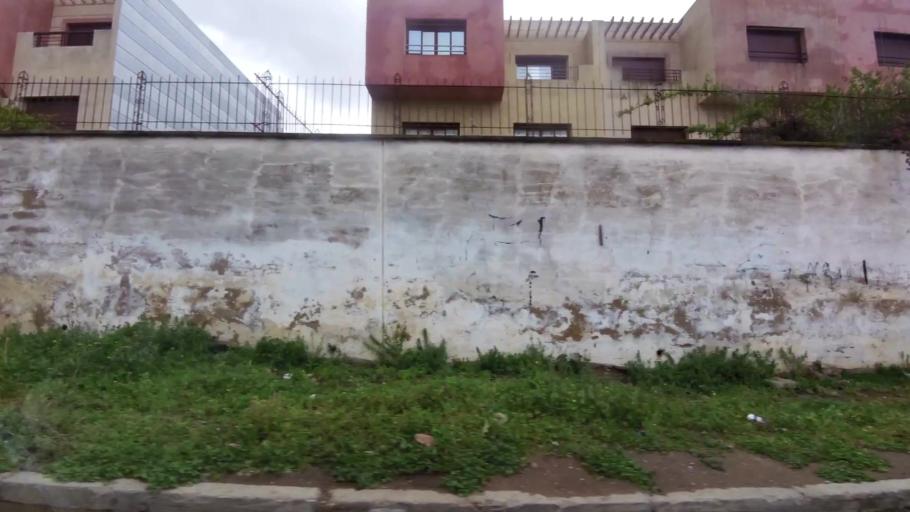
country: MA
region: Grand Casablanca
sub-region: Casablanca
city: Casablanca
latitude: 33.5702
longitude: -7.6895
